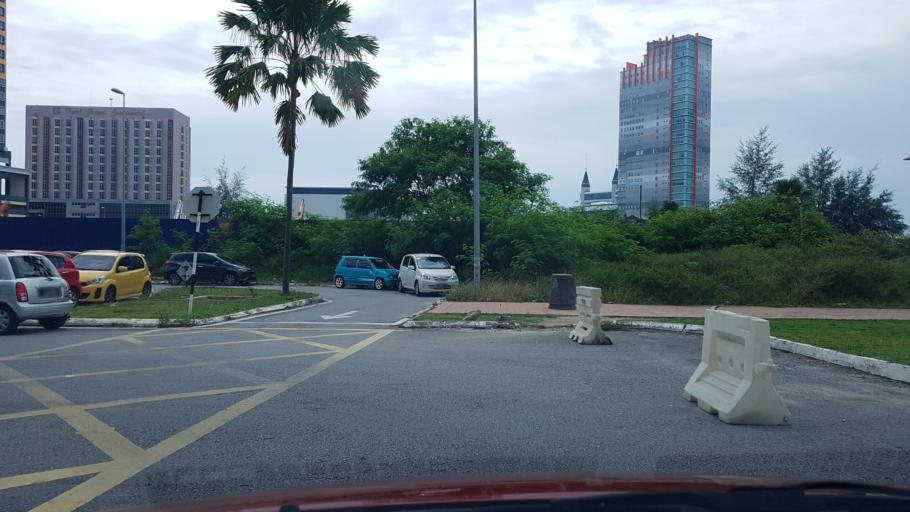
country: MY
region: Terengganu
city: Kuala Terengganu
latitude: 5.3351
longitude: 103.1494
